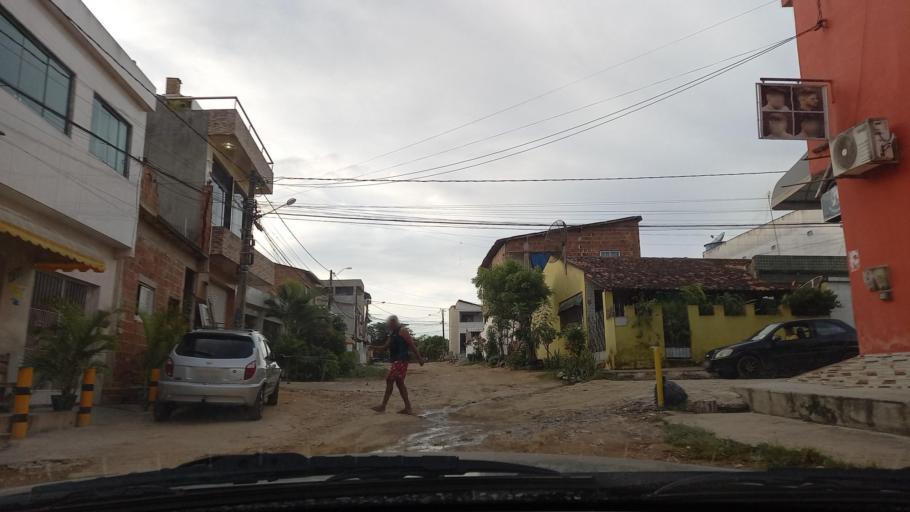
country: BR
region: Pernambuco
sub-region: Gravata
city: Gravata
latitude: -8.1956
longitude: -35.5766
